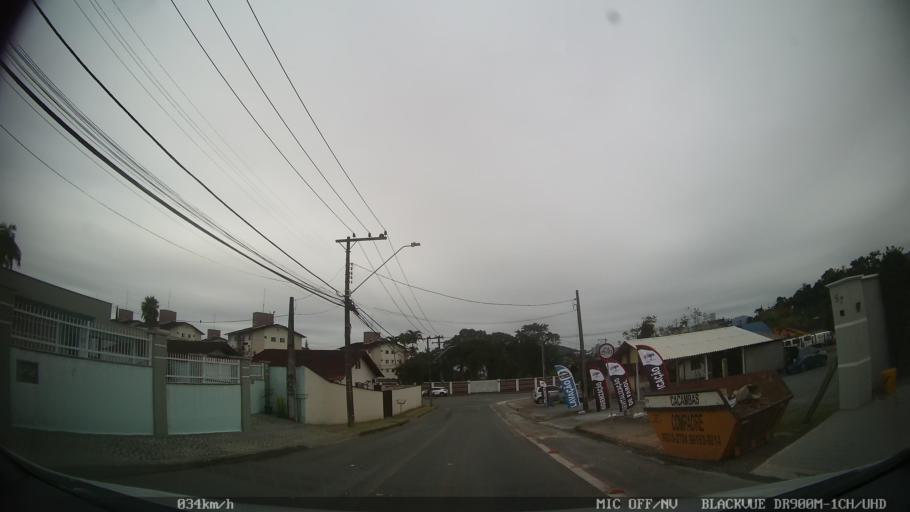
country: BR
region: Santa Catarina
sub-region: Joinville
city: Joinville
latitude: -26.2723
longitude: -48.8410
